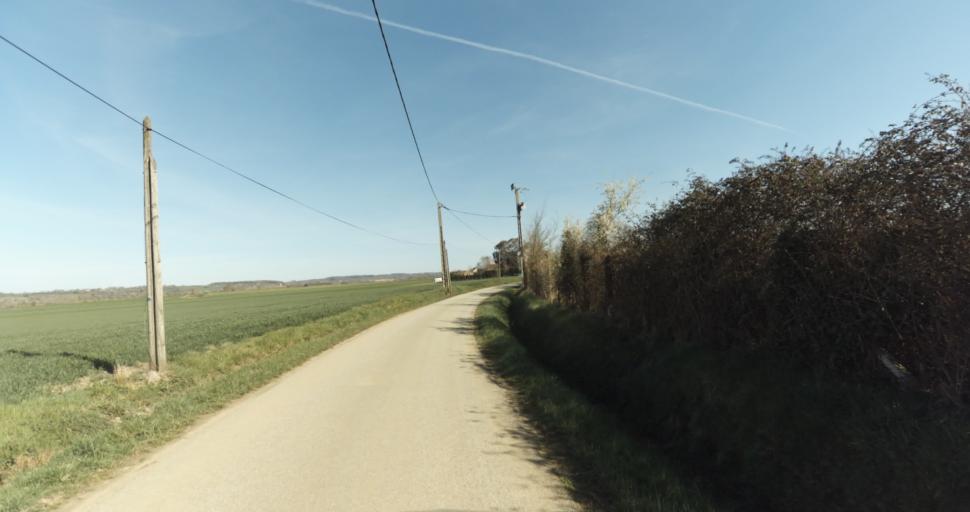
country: FR
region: Lower Normandy
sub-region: Departement du Calvados
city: Saint-Pierre-sur-Dives
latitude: 49.0387
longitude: -0.0102
